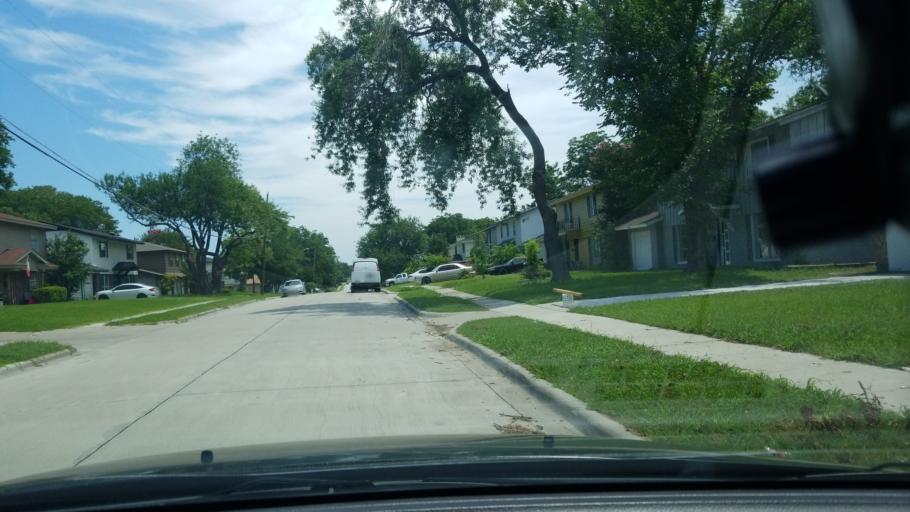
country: US
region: Texas
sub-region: Dallas County
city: Mesquite
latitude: 32.8034
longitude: -96.6559
